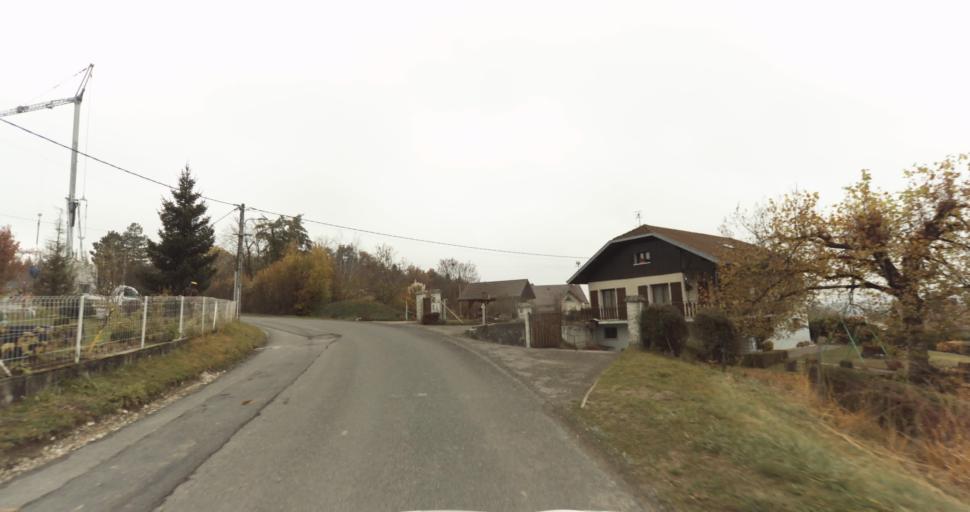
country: FR
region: Rhone-Alpes
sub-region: Departement de la Haute-Savoie
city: Cusy
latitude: 45.7737
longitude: 6.0141
